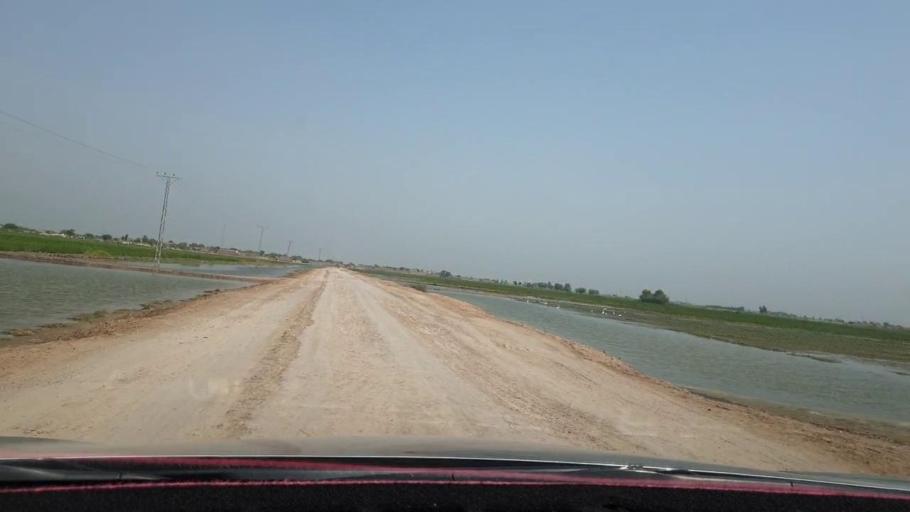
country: PK
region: Sindh
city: Warah
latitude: 27.4409
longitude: 67.7676
